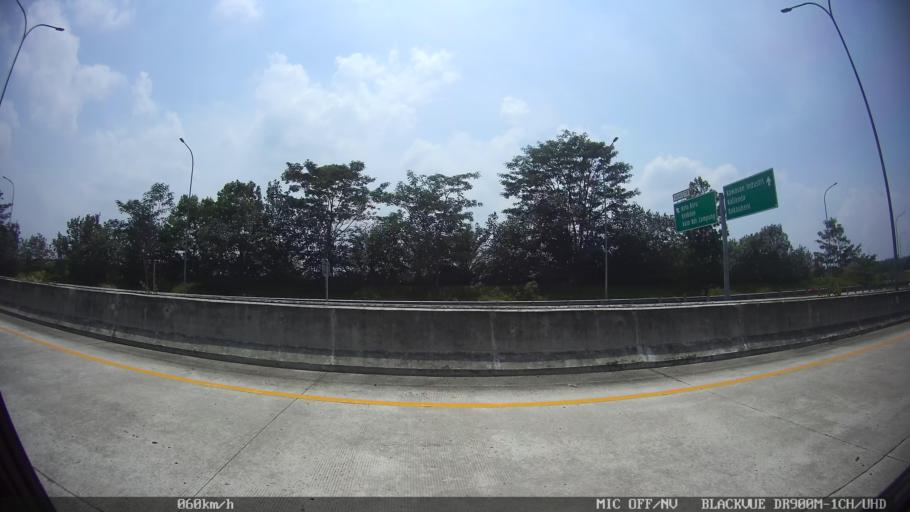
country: ID
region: Lampung
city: Kedaton
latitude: -5.3647
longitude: 105.3258
